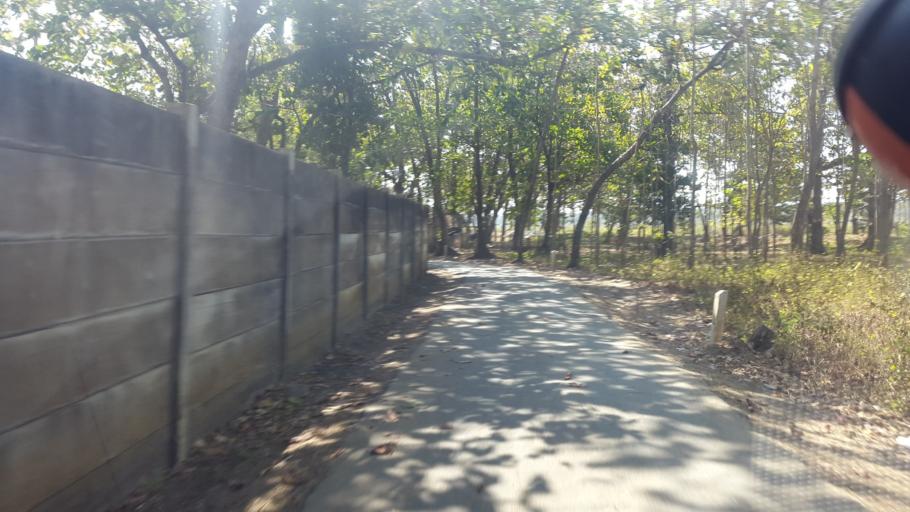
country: ID
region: West Java
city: Gunungbatu
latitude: -7.3298
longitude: 106.3983
